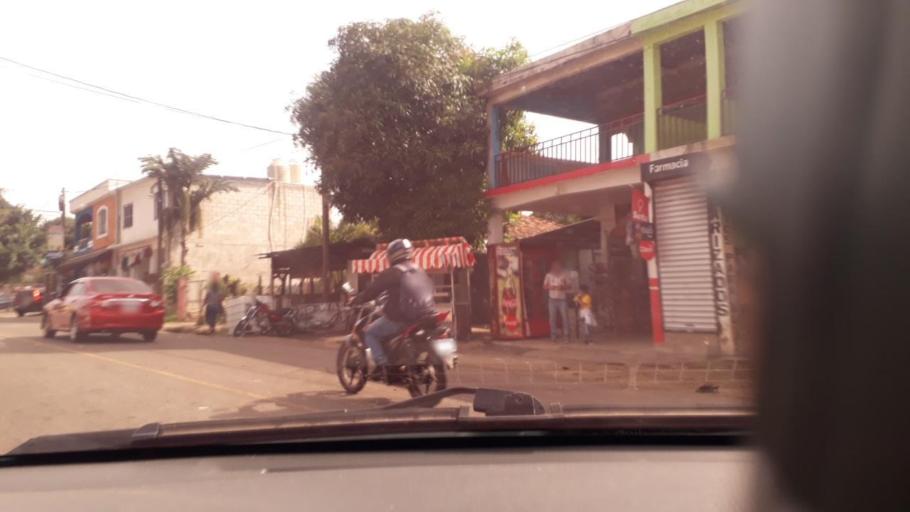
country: GT
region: Jutiapa
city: Quesada
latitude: 14.2417
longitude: -90.0294
